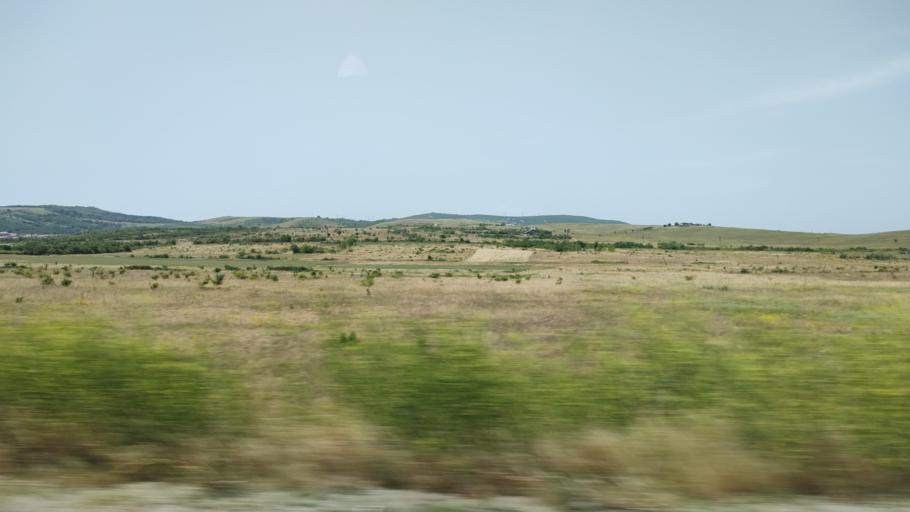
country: RO
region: Mehedinti
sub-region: Comuna Breznita Ocol
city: Breznita Ocol
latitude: 44.6375
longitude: 22.6123
